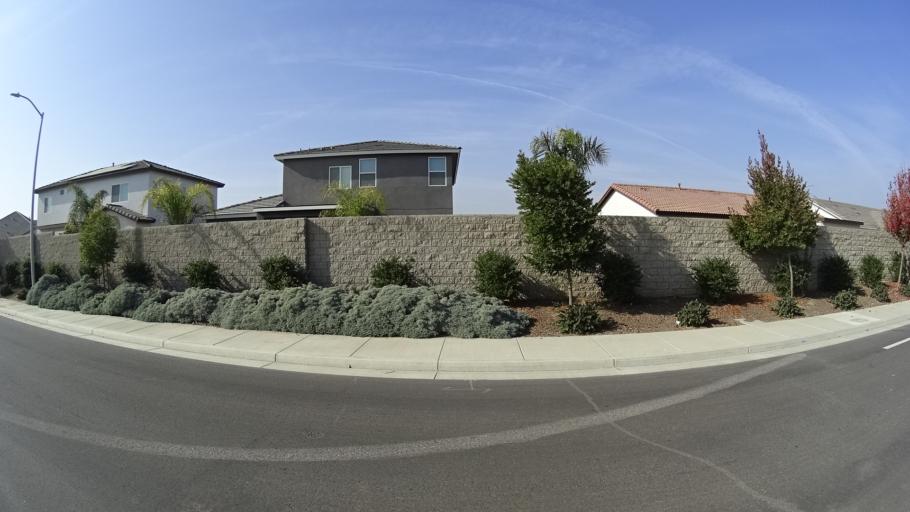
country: US
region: California
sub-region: Kern County
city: Greenacres
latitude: 35.2900
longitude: -119.1100
